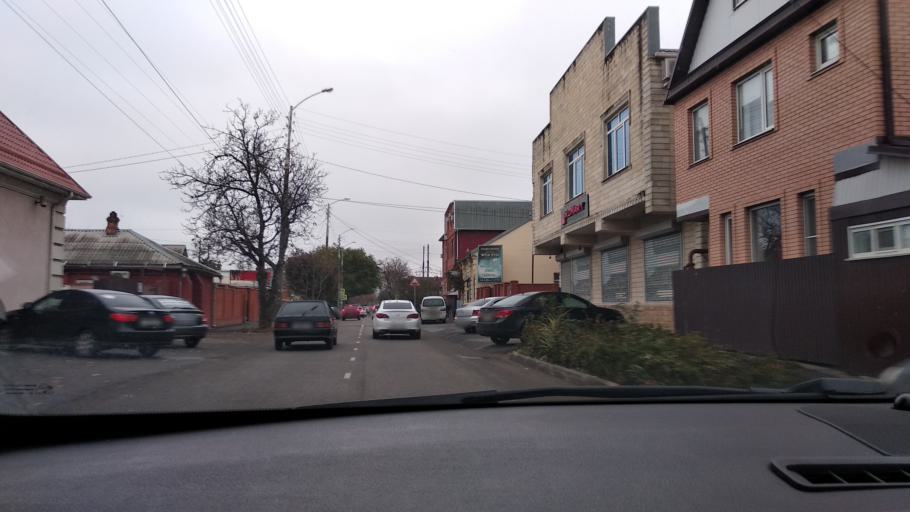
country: RU
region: Krasnodarskiy
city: Krasnodar
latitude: 45.0280
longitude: 38.9871
